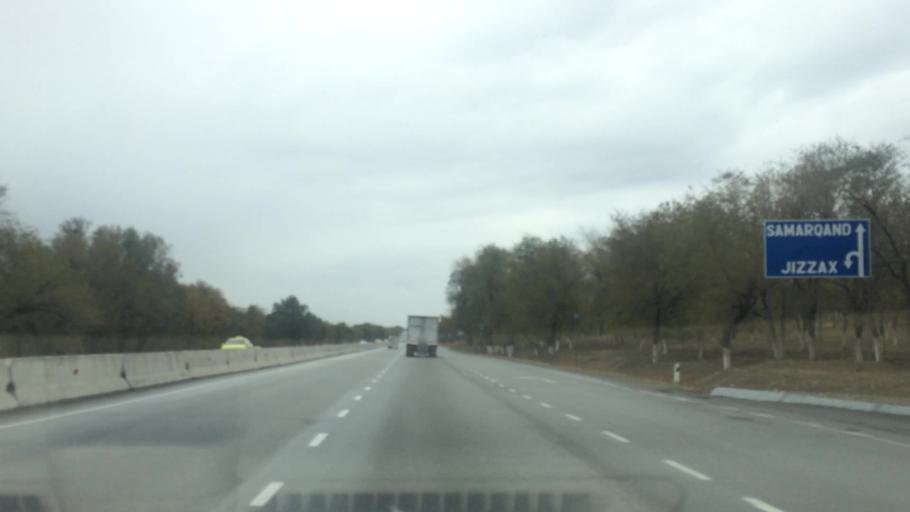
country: UZ
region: Samarqand
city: Bulung'ur
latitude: 39.9028
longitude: 67.5028
